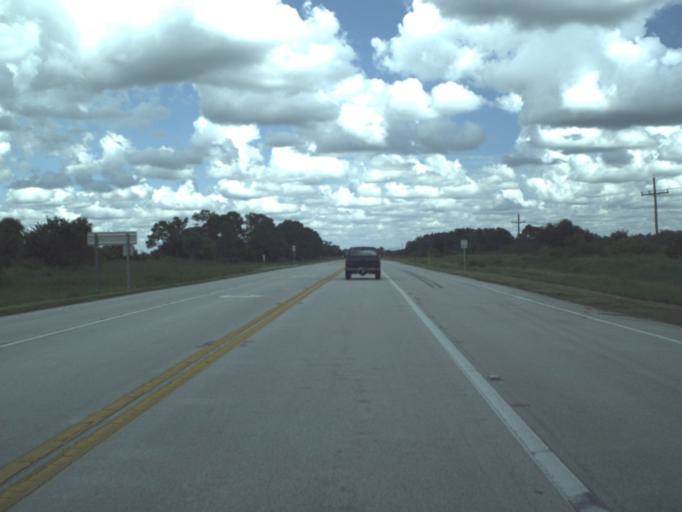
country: US
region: Florida
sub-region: Hendry County
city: Port LaBelle
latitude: 26.5967
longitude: -81.4367
